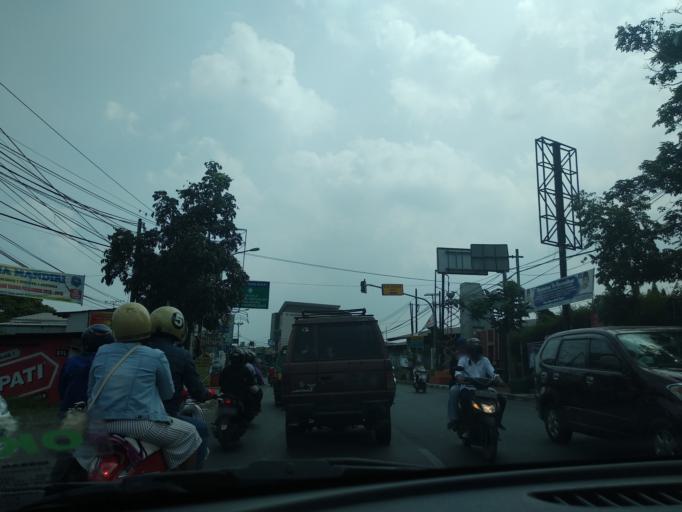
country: ID
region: West Java
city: Cimahi
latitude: -6.8686
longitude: 107.5263
